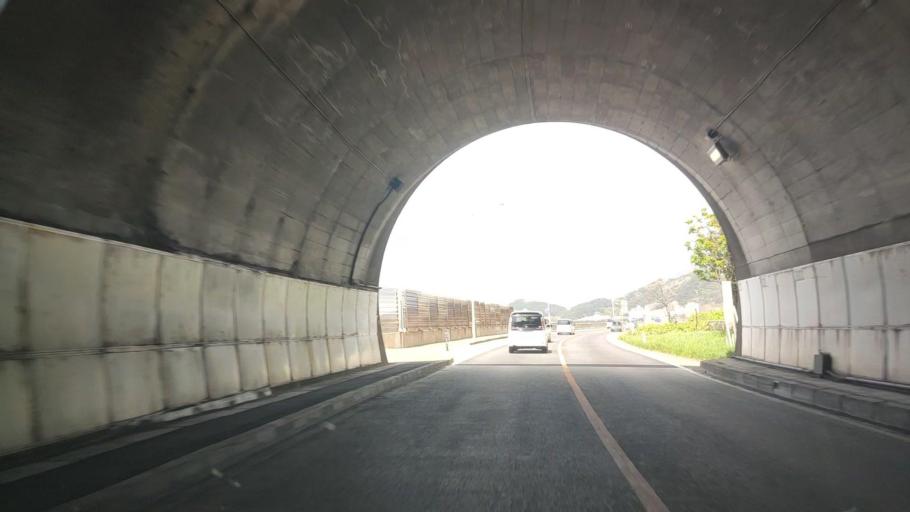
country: JP
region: Aomori
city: Aomori Shi
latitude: 40.8835
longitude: 140.8508
